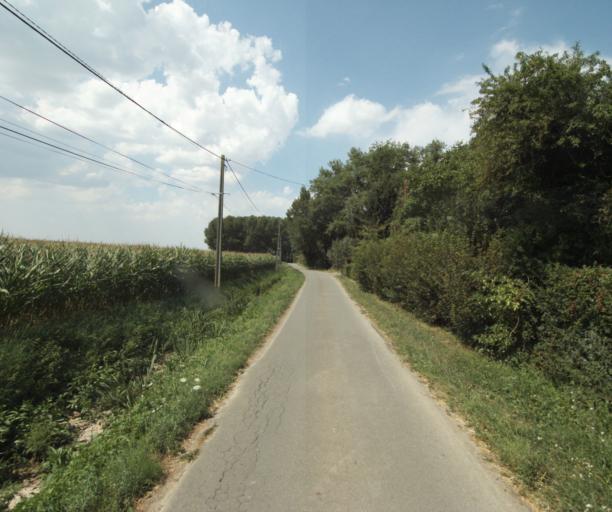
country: FR
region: Nord-Pas-de-Calais
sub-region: Departement du Nord
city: Comines
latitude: 50.7473
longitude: 2.9985
